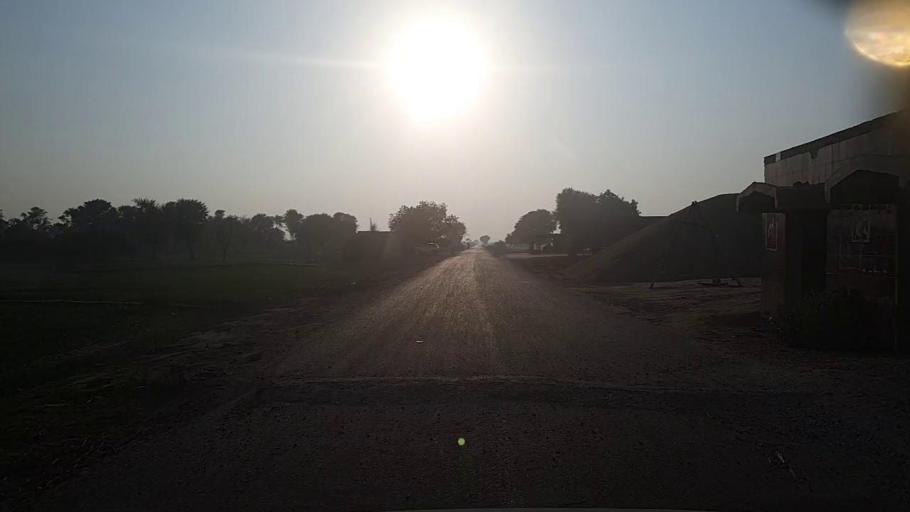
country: PK
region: Sindh
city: Pad Idan
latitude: 26.7147
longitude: 68.3995
